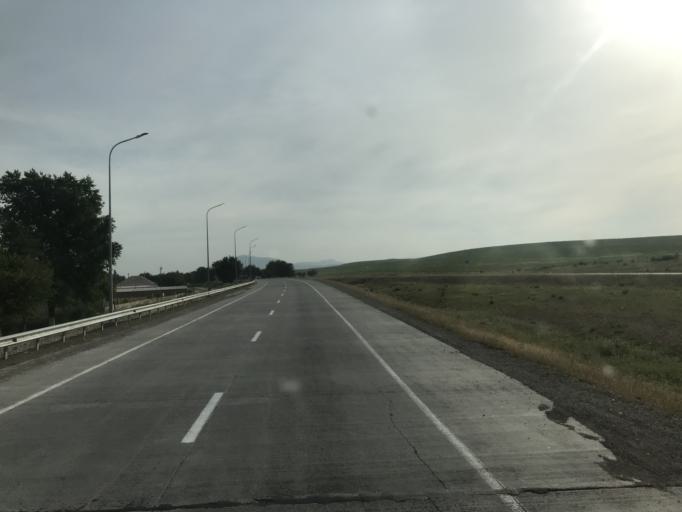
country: KZ
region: Ongtustik Qazaqstan
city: Qazyqurt
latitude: 41.9007
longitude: 69.4600
